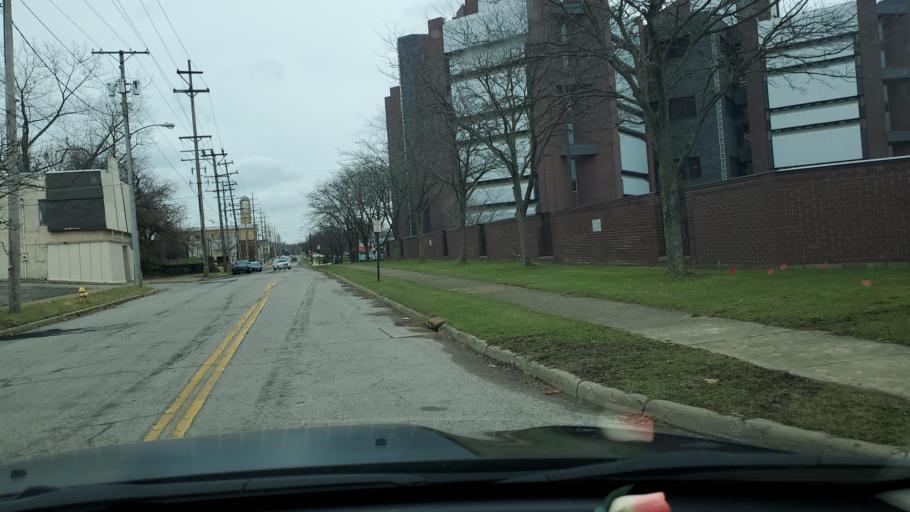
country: US
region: Ohio
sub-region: Mahoning County
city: Youngstown
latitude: 41.1051
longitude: -80.6556
